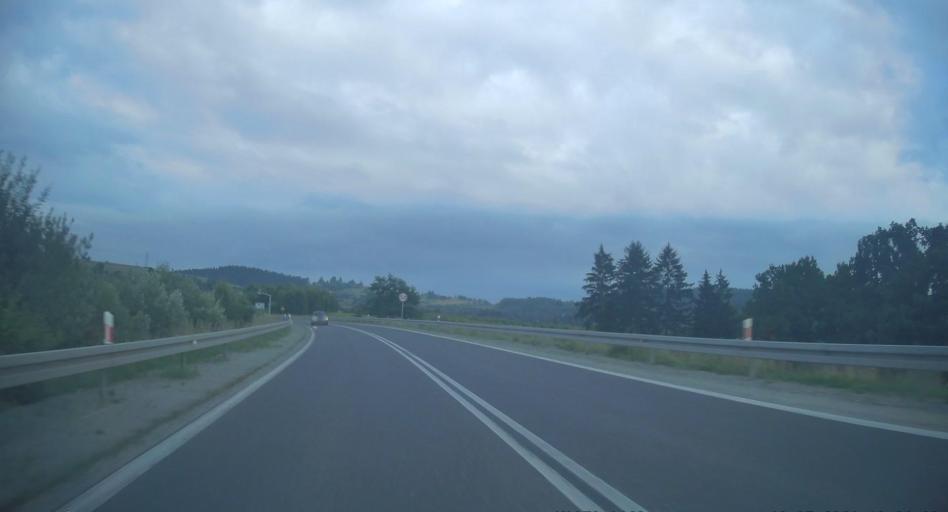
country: PL
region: Lower Silesian Voivodeship
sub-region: Powiat klodzki
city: Nowa Ruda
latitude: 50.5987
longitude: 16.5133
